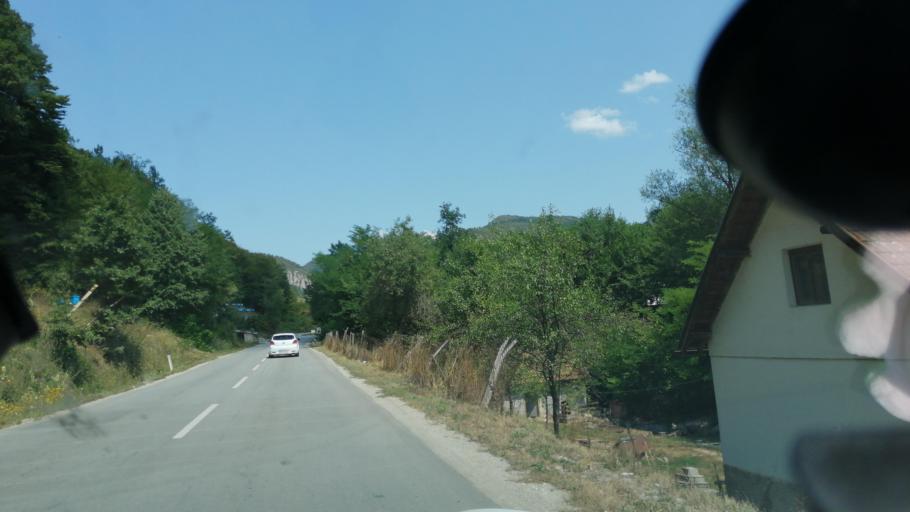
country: RS
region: Central Serbia
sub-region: Moravicki Okrug
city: Ivanjica
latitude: 43.6099
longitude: 20.2353
